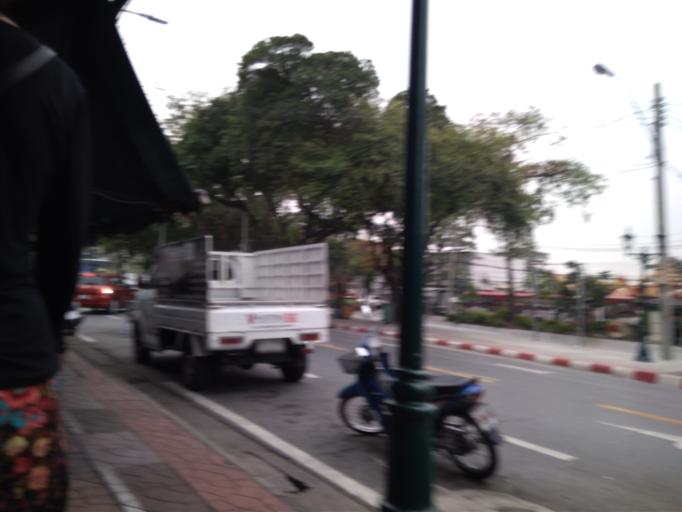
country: TH
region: Bangkok
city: Bangkok
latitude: 13.7464
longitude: 100.4965
